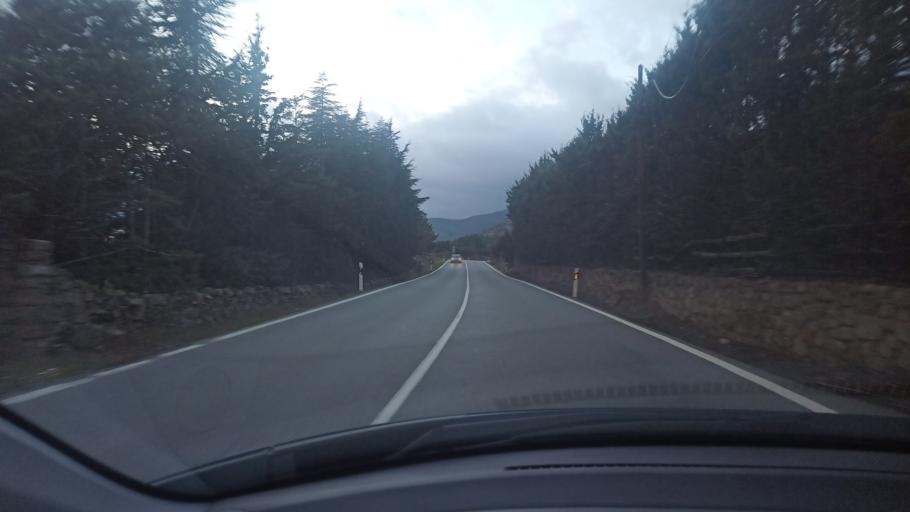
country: ES
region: Madrid
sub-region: Provincia de Madrid
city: El Escorial
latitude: 40.5390
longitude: -4.1368
